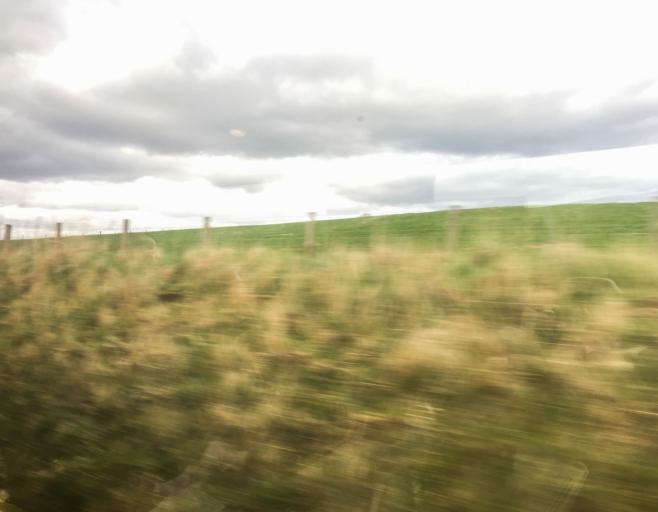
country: GB
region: Scotland
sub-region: South Lanarkshire
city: Carnwath
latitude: 55.6510
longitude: -3.6339
